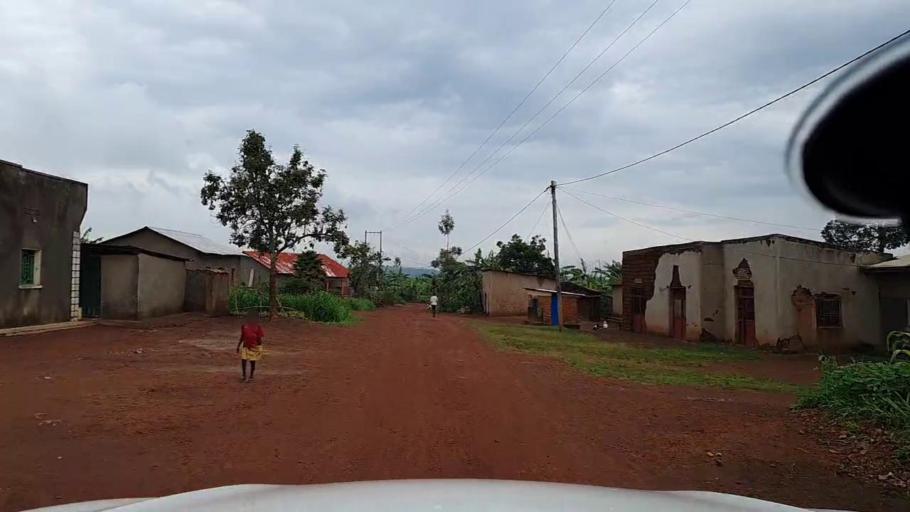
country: RW
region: Kigali
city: Kigali
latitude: -1.9265
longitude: 29.8997
